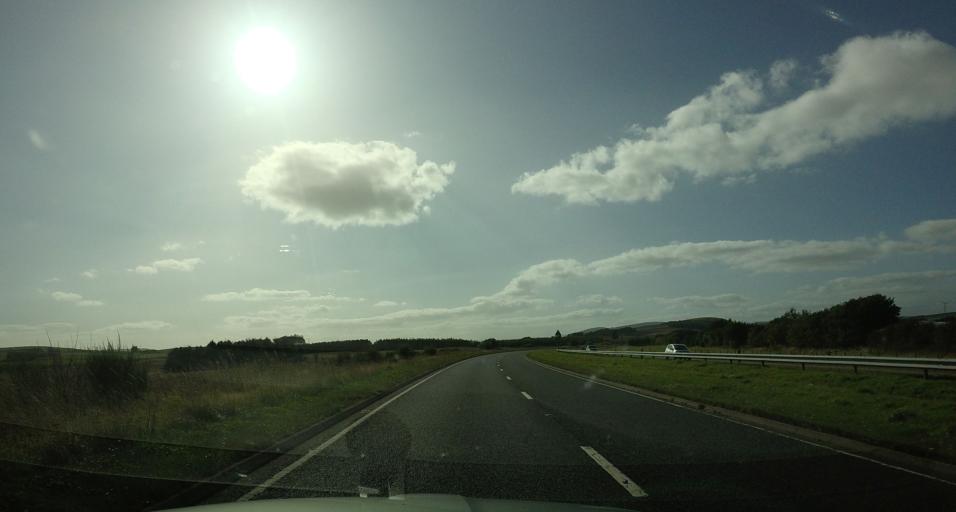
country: GB
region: Scotland
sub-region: Aberdeenshire
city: Inverbervie
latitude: 56.9107
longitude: -2.3408
